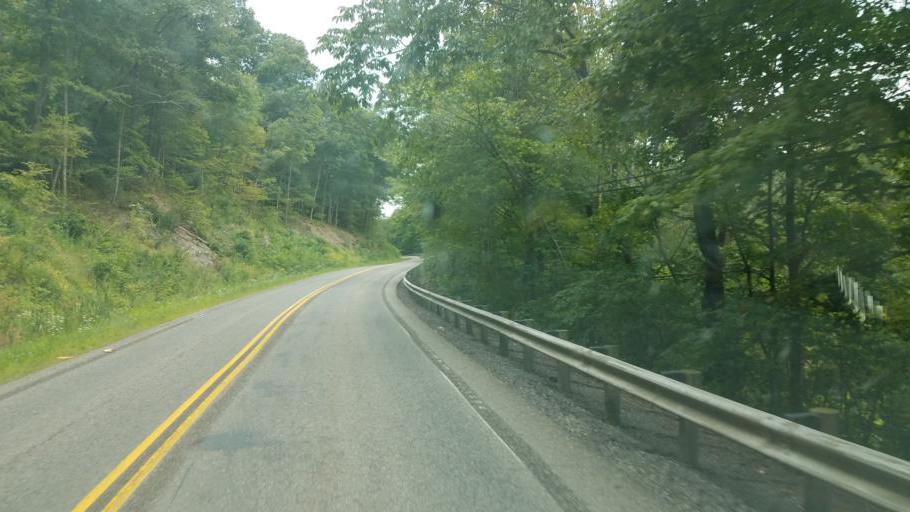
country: US
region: Ohio
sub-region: Columbiana County
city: Lisbon
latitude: 40.7723
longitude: -80.6965
